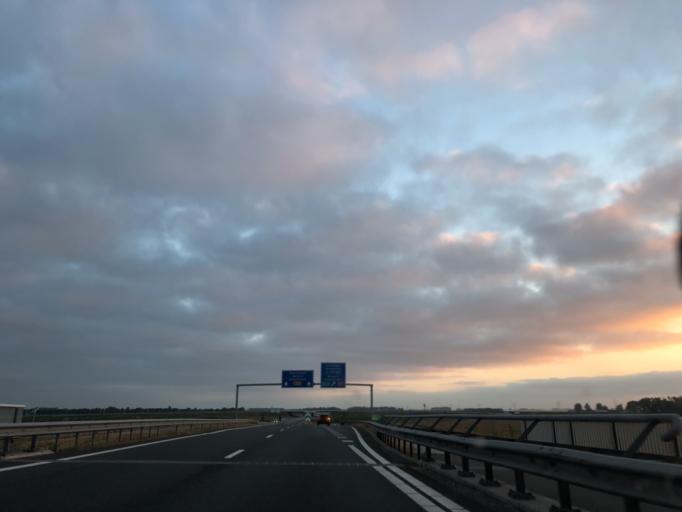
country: NL
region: Groningen
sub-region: Gemeente Veendam
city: Veendam
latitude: 53.1645
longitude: 6.8951
